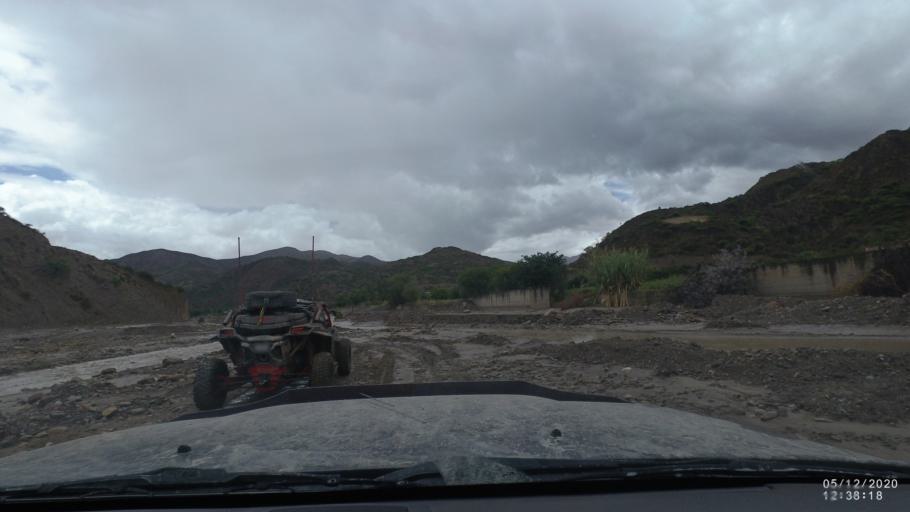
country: BO
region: Cochabamba
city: Sipe Sipe
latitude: -17.5439
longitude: -66.4237
